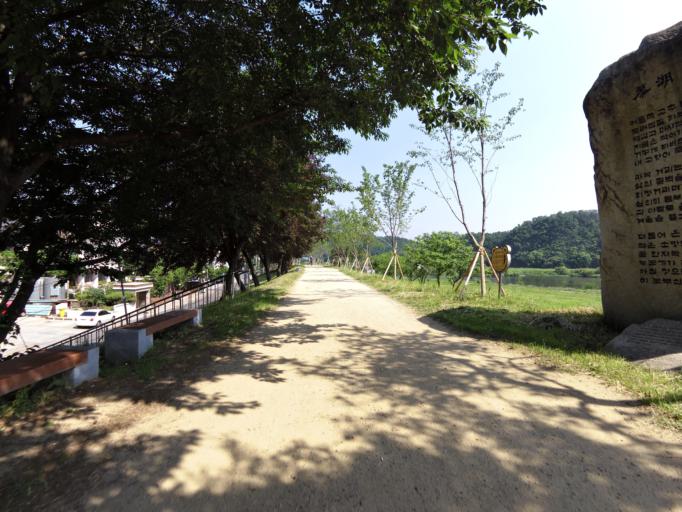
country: KR
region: Daegu
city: Daegu
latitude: 35.8755
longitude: 128.6634
